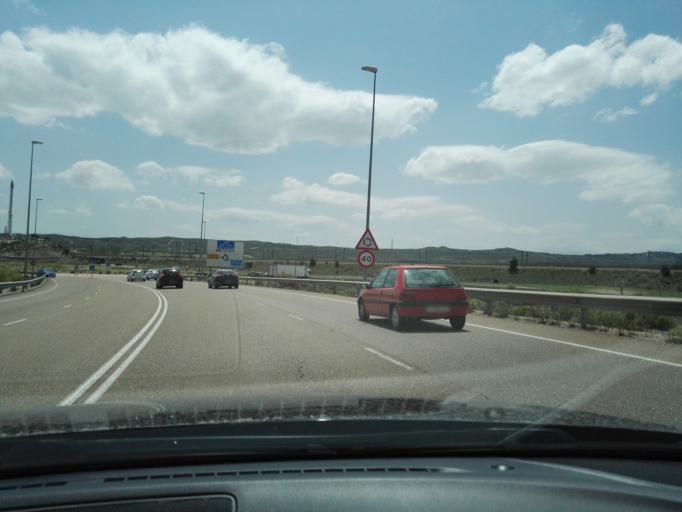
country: ES
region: Aragon
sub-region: Provincia de Zaragoza
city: Montecanal
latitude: 41.6293
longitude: -0.9903
